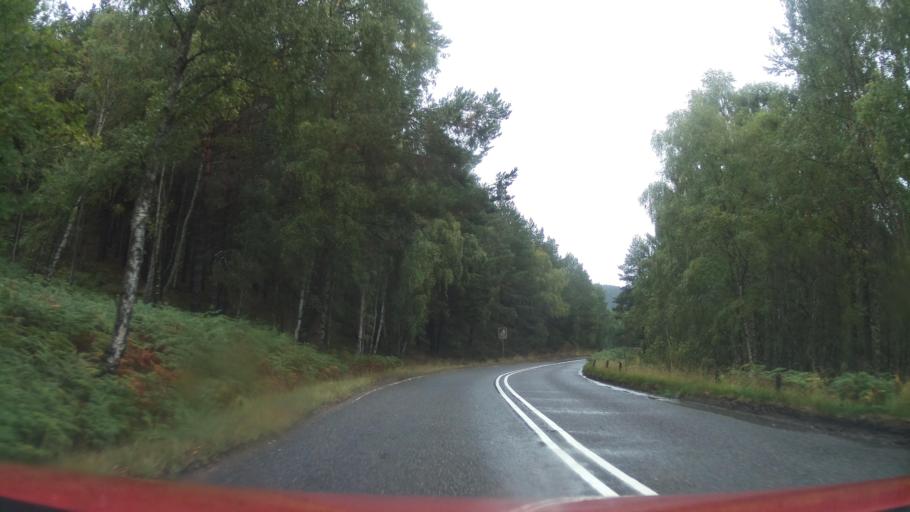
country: GB
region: Scotland
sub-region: Aberdeenshire
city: Ballater
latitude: 57.0574
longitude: -3.1309
